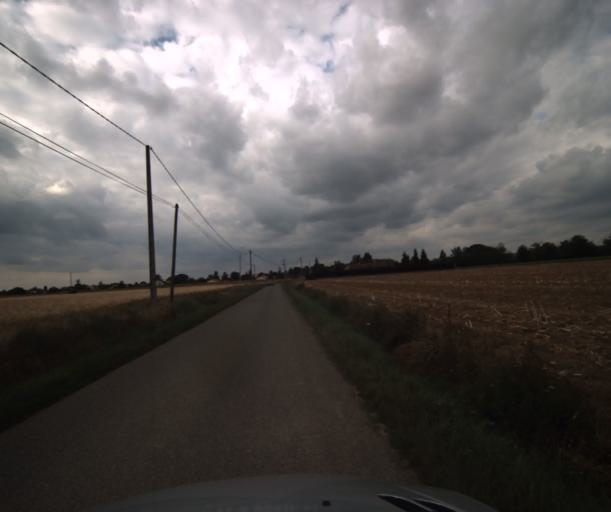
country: FR
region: Midi-Pyrenees
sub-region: Departement de la Haute-Garonne
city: Labarthe-sur-Leze
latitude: 43.4390
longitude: 1.3962
